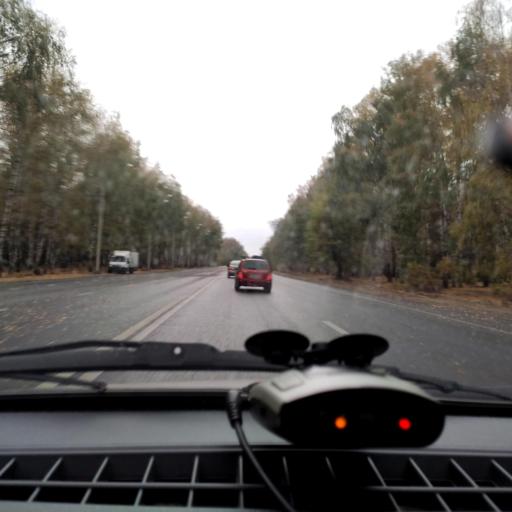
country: RU
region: Voronezj
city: Pridonskoy
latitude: 51.6900
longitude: 39.1023
